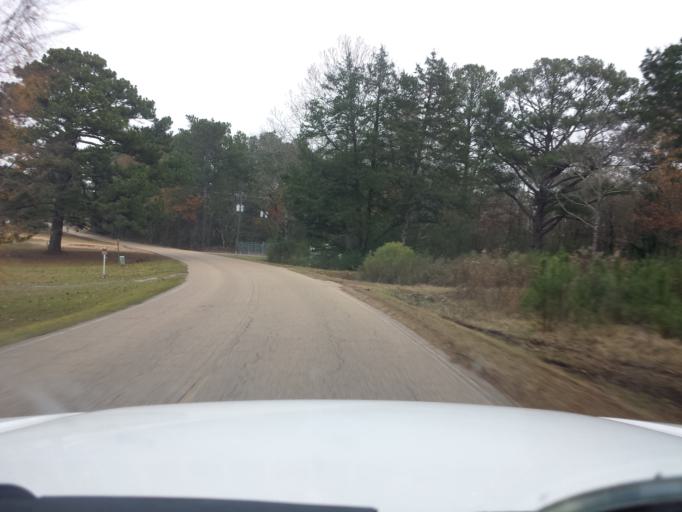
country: US
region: Mississippi
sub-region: Rankin County
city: Brandon
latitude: 32.4193
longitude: -89.9535
